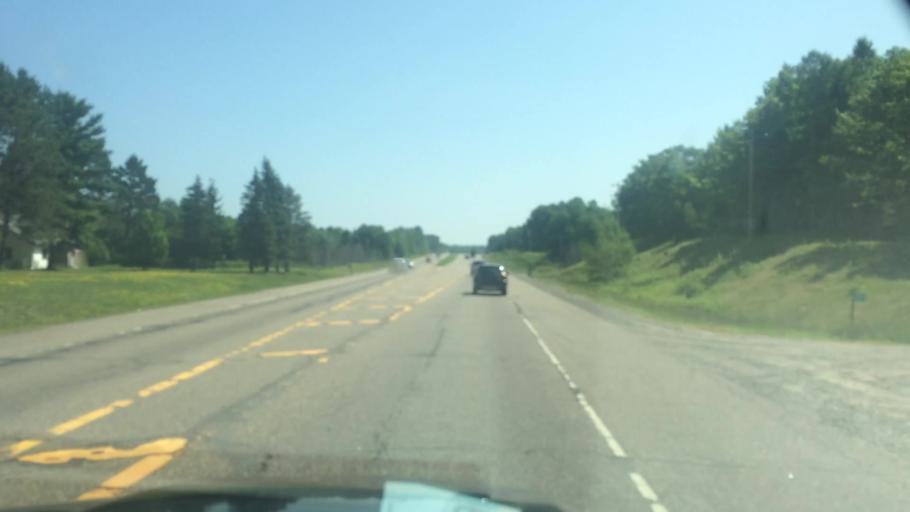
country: US
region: Wisconsin
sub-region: Oneida County
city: Rhinelander
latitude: 45.6174
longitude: -89.4925
